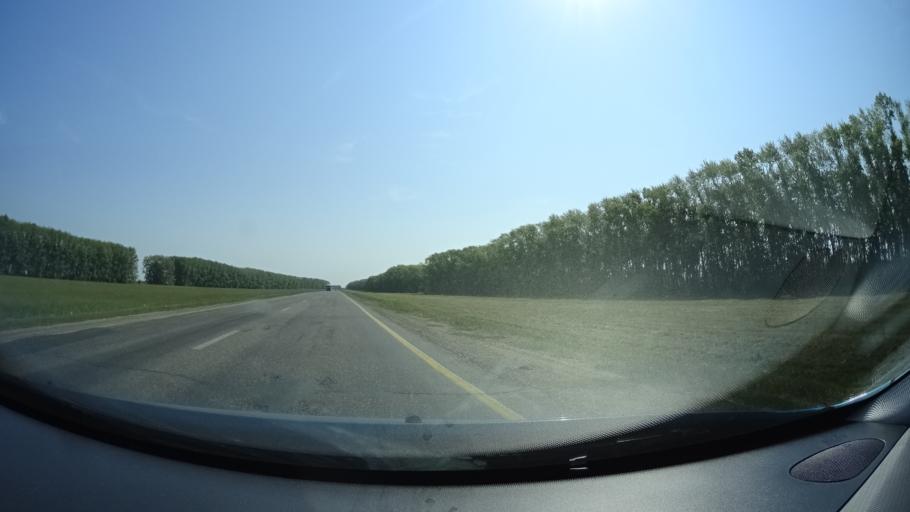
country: RU
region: Bashkortostan
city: Karmaskaly
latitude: 54.3951
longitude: 56.1096
